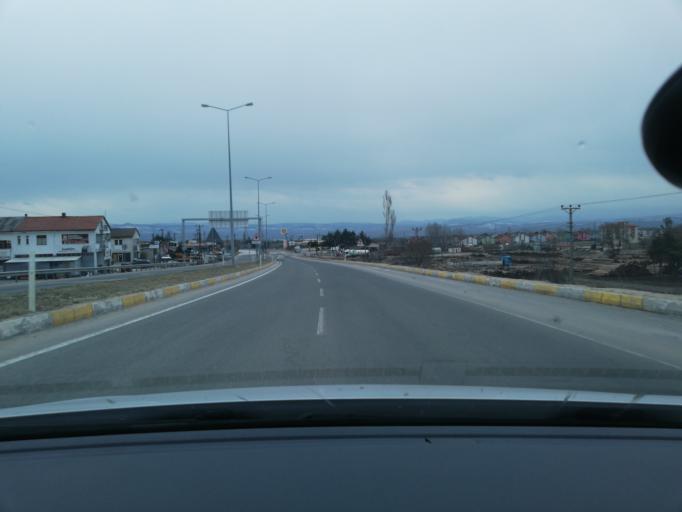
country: TR
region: Bolu
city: Gerede
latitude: 40.7902
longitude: 32.2083
